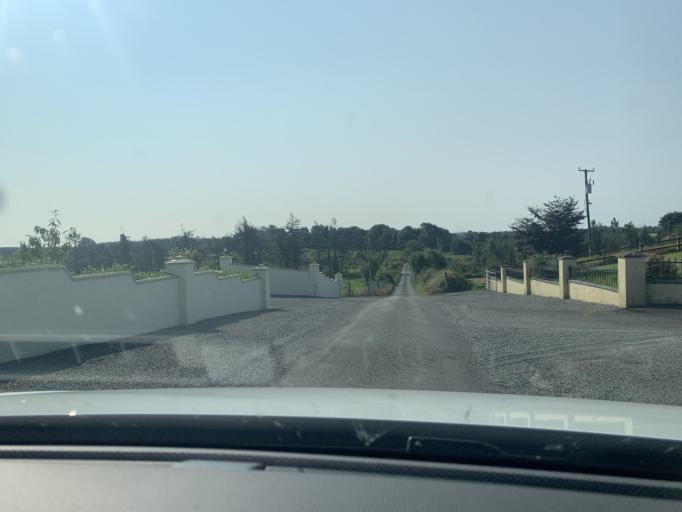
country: IE
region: Connaught
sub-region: Maigh Eo
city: Ballyhaunis
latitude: 53.7847
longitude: -8.7403
